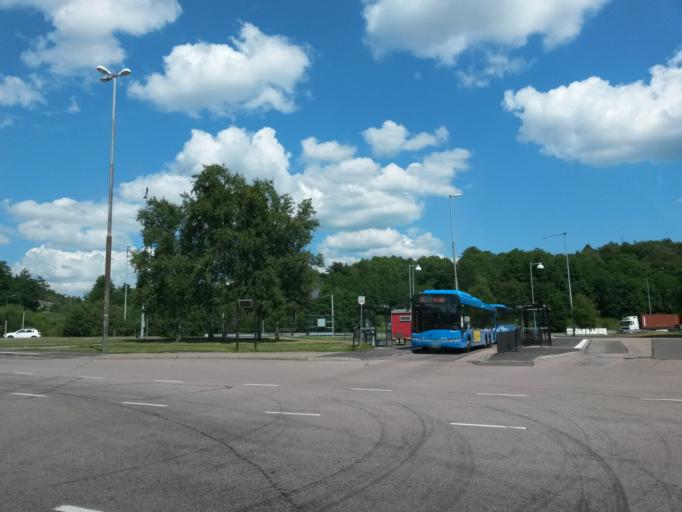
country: SE
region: Vaestra Goetaland
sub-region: Ale Kommun
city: Surte
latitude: 57.7998
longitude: 11.9918
